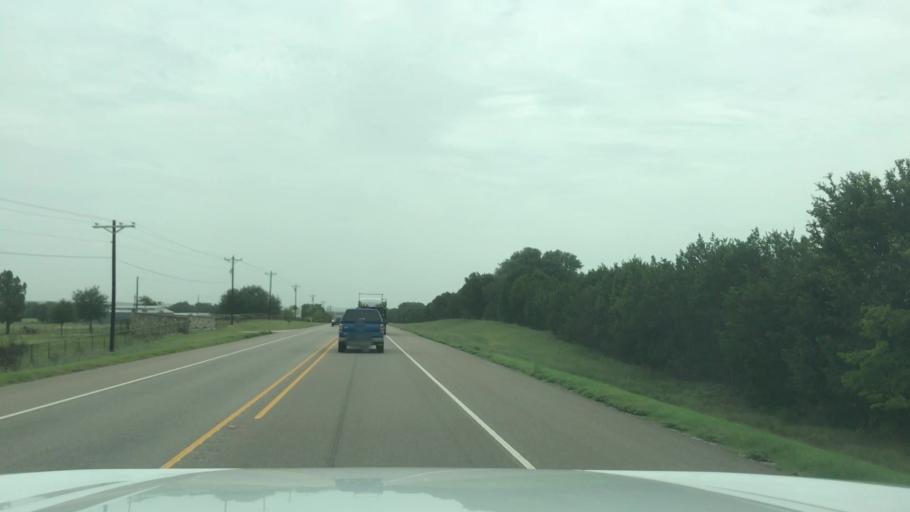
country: US
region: Texas
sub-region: Bosque County
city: Meridian
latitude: 31.9323
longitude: -97.6960
